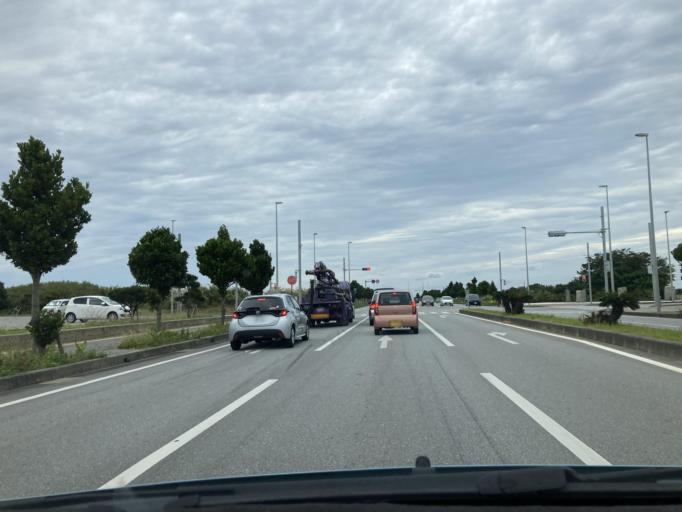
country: JP
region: Okinawa
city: Okinawa
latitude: 26.3934
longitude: 127.7442
